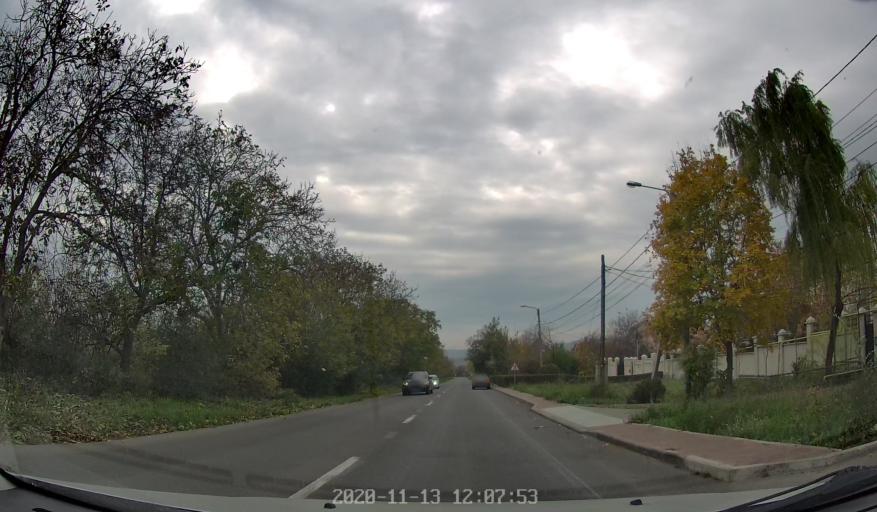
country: MD
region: Chisinau
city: Chisinau
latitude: 46.9707
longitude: 28.8337
